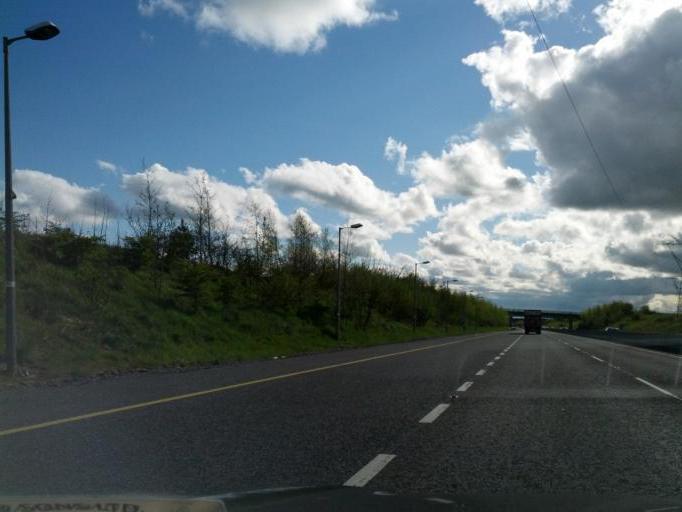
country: IE
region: Leinster
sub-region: An Iarmhi
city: Rochfortbridge
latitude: 53.3853
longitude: -7.3682
